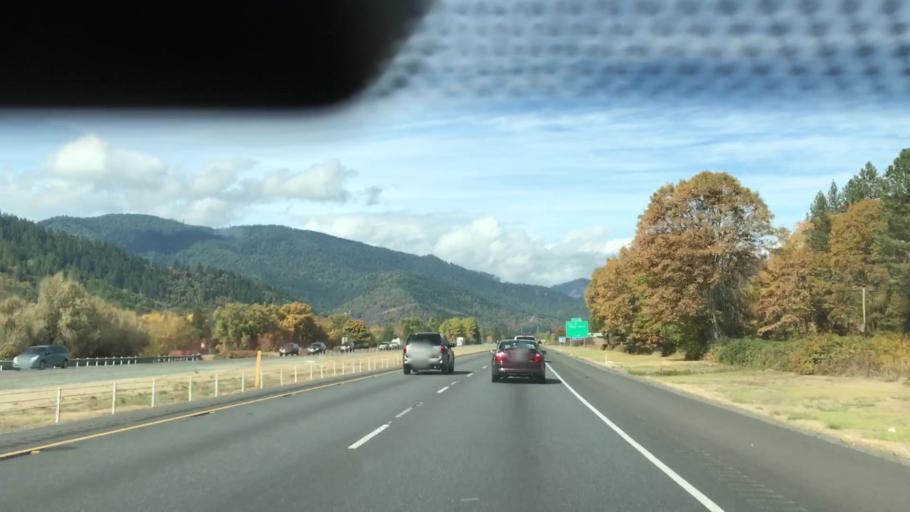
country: US
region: Oregon
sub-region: Jackson County
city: Rogue River
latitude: 42.4153
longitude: -123.1561
